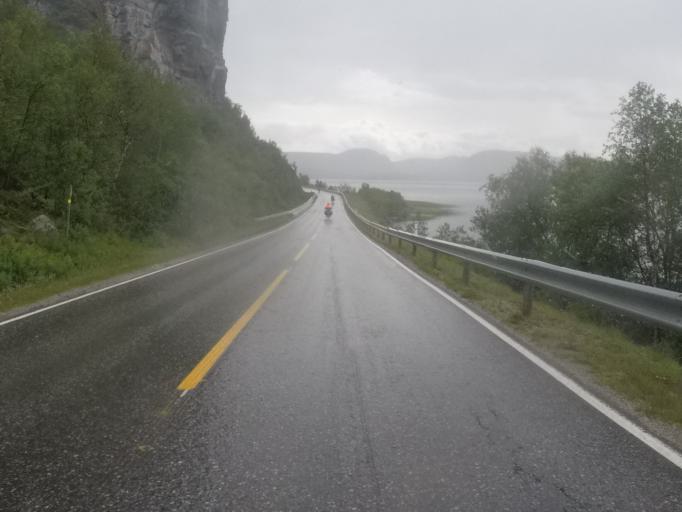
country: NO
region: Finnmark Fylke
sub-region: Porsanger
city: Lakselv
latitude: 69.8571
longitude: 25.0500
